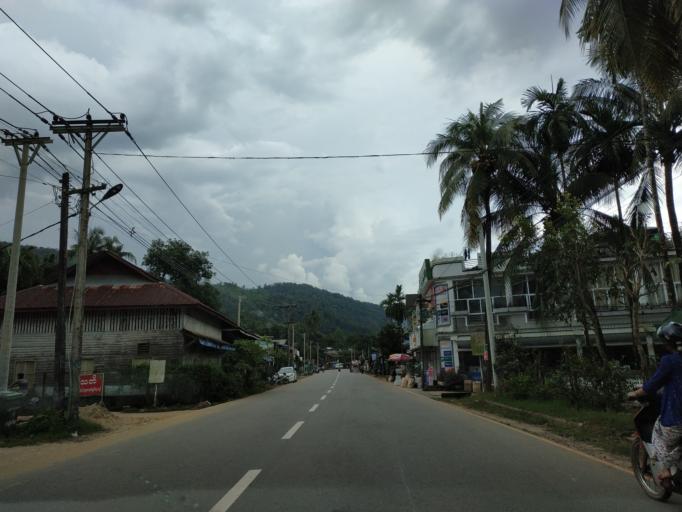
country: MM
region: Tanintharyi
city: Dawei
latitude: 13.8607
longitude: 98.2655
